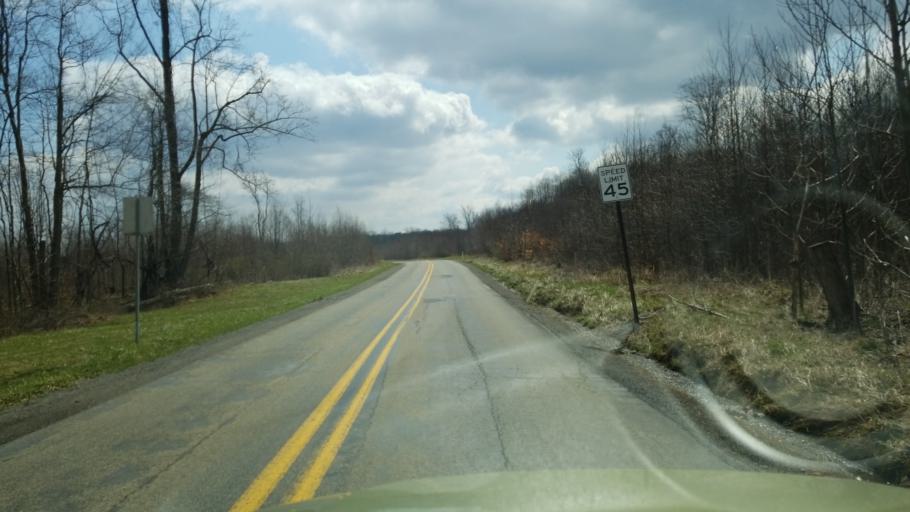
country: US
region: Pennsylvania
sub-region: Jefferson County
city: Brockway
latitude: 41.2795
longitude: -78.8677
